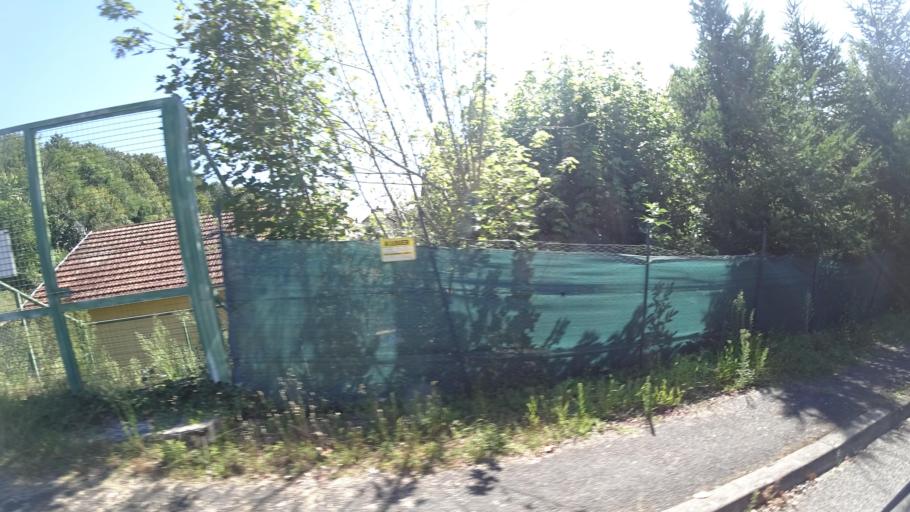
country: FR
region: Midi-Pyrenees
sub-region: Departement de l'Aveyron
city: Cransac
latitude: 44.5268
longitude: 2.2794
